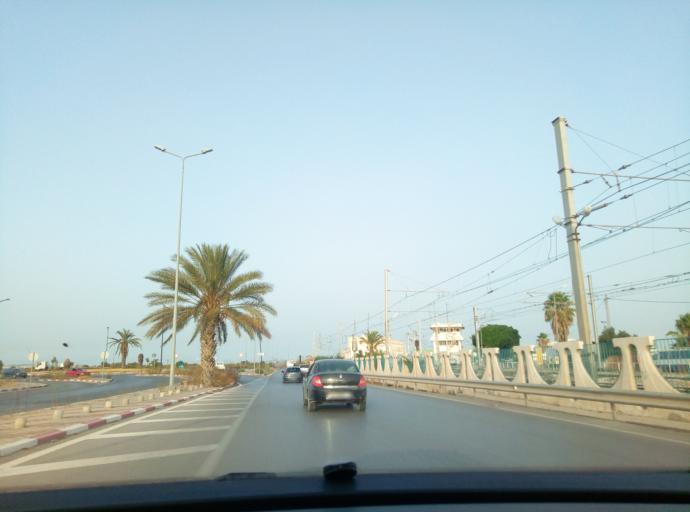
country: TN
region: Tunis
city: Tunis
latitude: 36.8011
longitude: 10.1940
